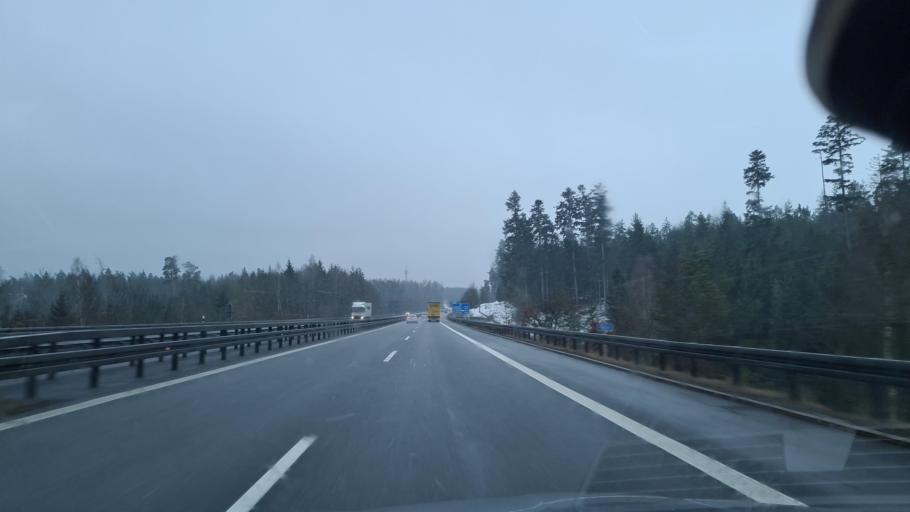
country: DE
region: Bavaria
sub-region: Upper Palatinate
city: Berg
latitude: 49.8538
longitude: 12.1792
